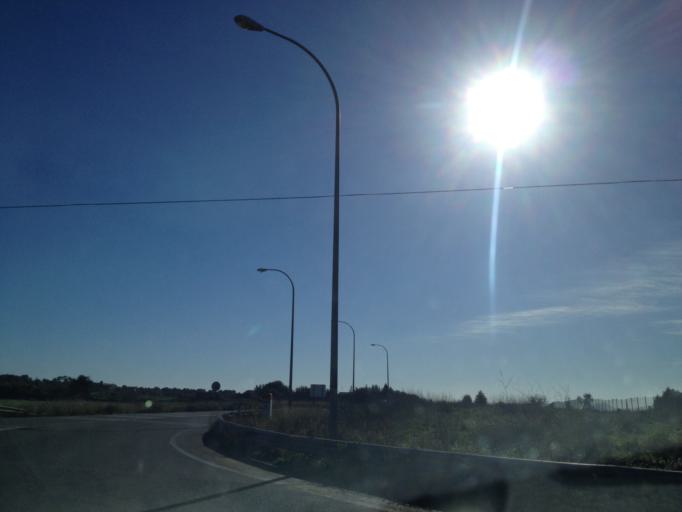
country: ES
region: Balearic Islands
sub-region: Illes Balears
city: Petra
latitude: 39.6169
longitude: 3.1217
